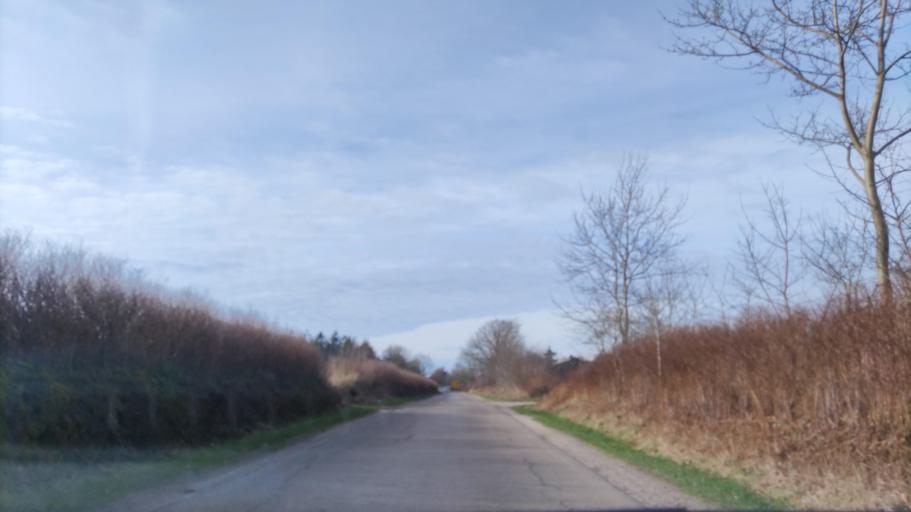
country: DE
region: Schleswig-Holstein
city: Kropp
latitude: 54.4126
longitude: 9.5361
